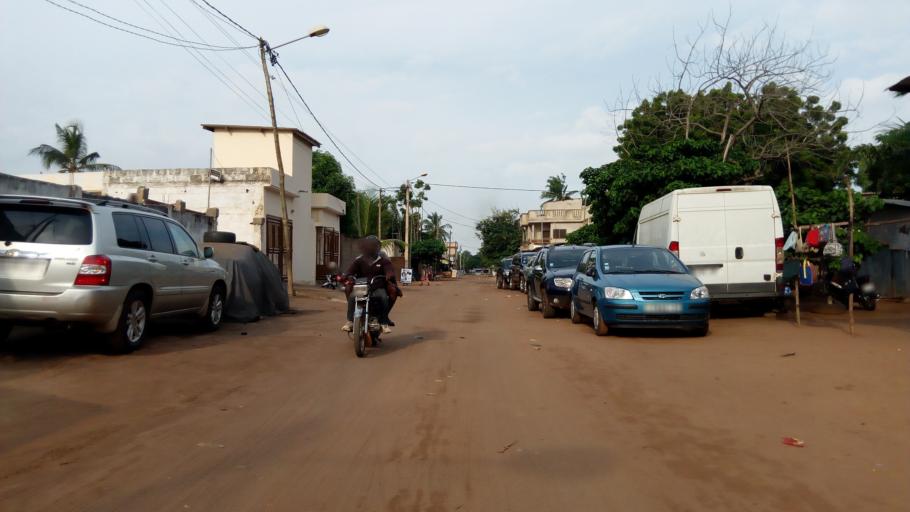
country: TG
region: Maritime
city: Lome
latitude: 6.2153
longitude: 1.2035
